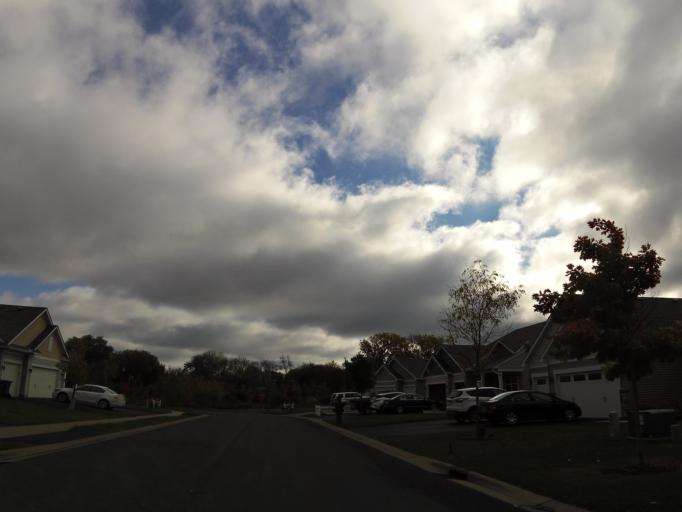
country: US
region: Minnesota
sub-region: Scott County
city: Savage
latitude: 44.7747
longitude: -93.3306
